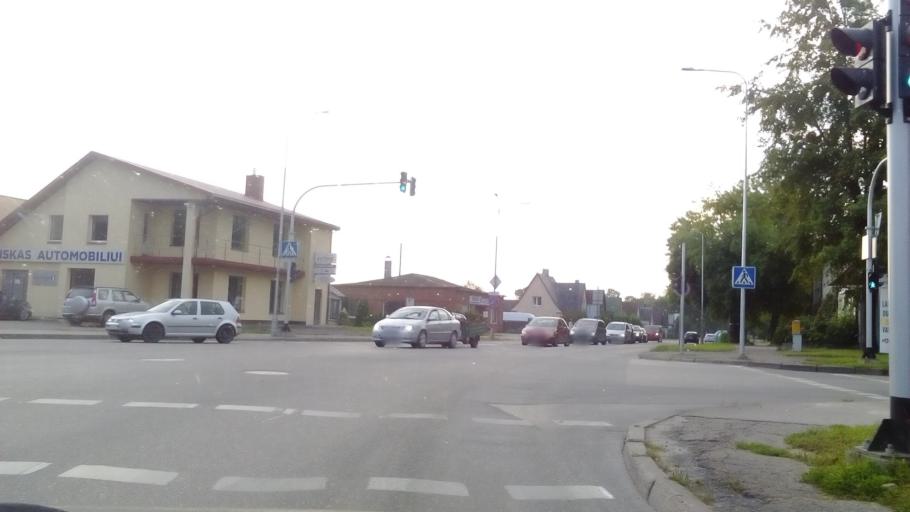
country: LT
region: Alytaus apskritis
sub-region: Alytus
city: Alytus
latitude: 54.3869
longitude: 24.0424
